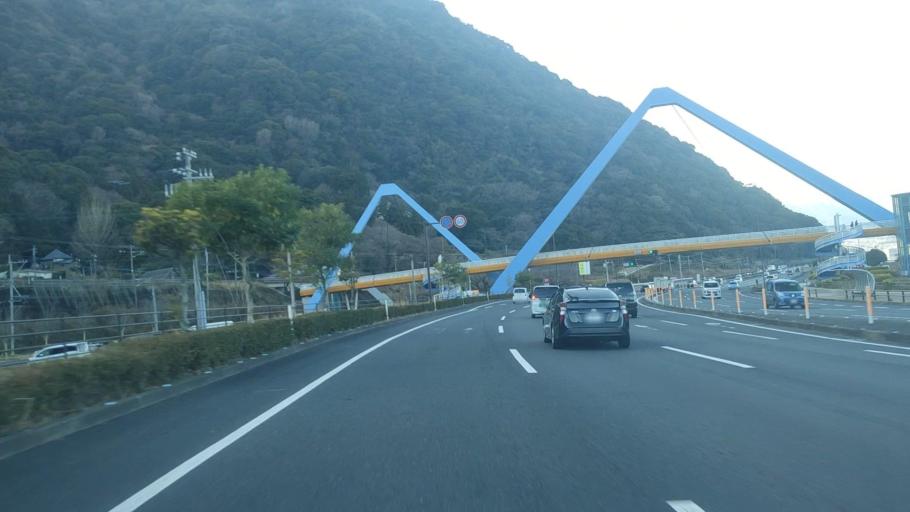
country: JP
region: Oita
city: Beppu
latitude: 33.2580
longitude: 131.5357
